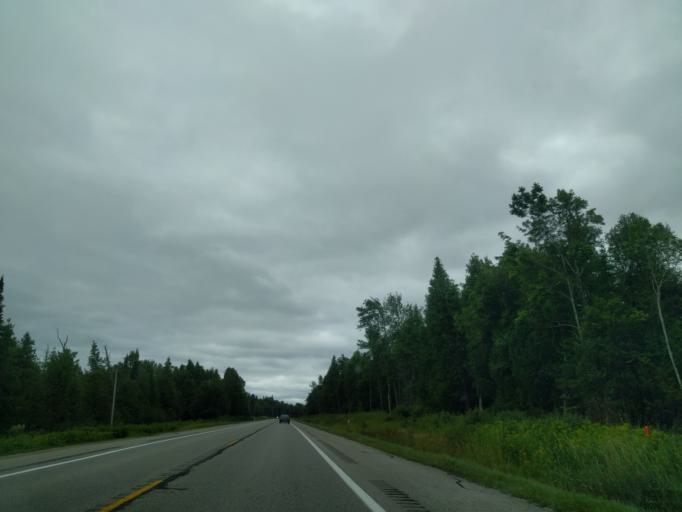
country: US
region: Michigan
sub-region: Delta County
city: Escanaba
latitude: 45.6590
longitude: -87.1756
